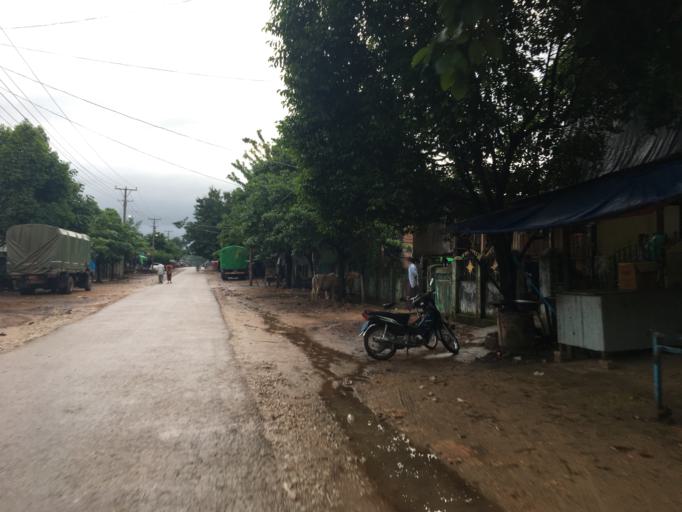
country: MM
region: Mon
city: Mudon
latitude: 16.0410
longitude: 98.1189
